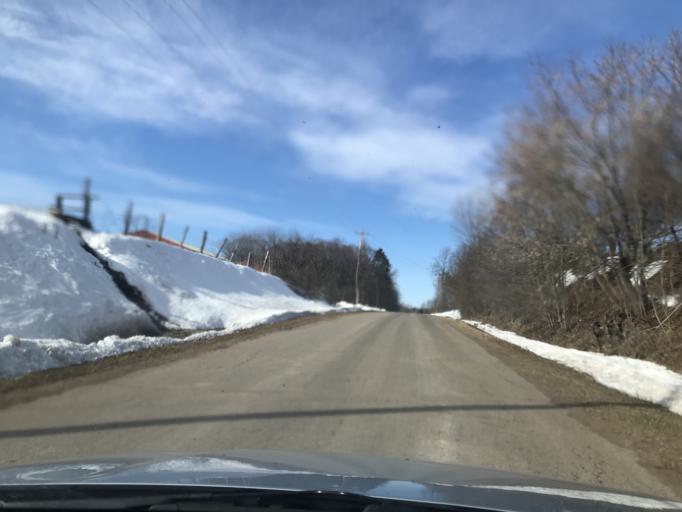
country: US
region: Wisconsin
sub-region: Oconto County
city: Gillett
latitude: 44.9618
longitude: -88.2986
